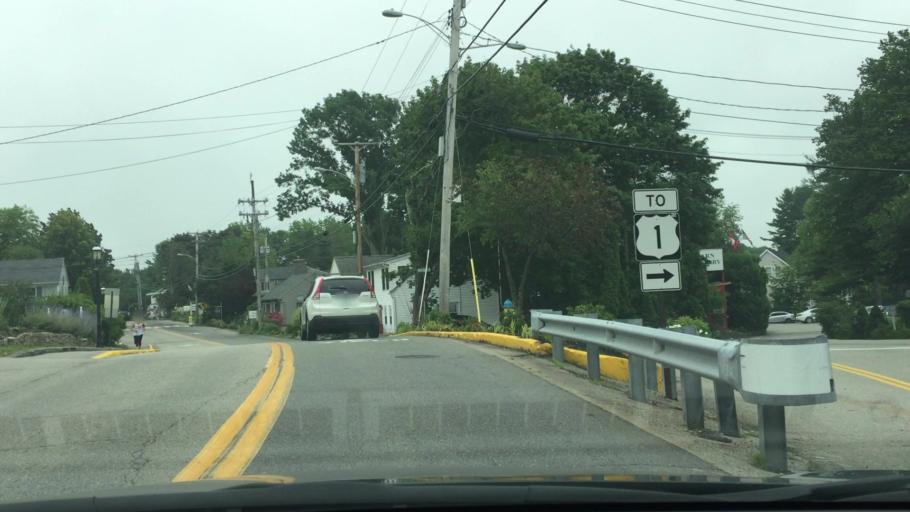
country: US
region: Maine
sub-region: York County
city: Ogunquit
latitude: 43.2420
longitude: -70.5970
